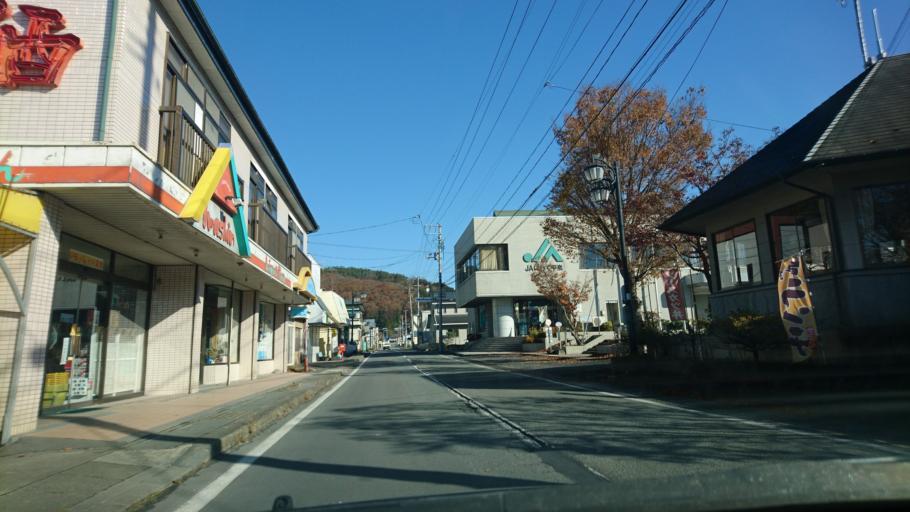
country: JP
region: Iwate
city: Ichinoseki
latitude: 38.9957
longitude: 141.2546
